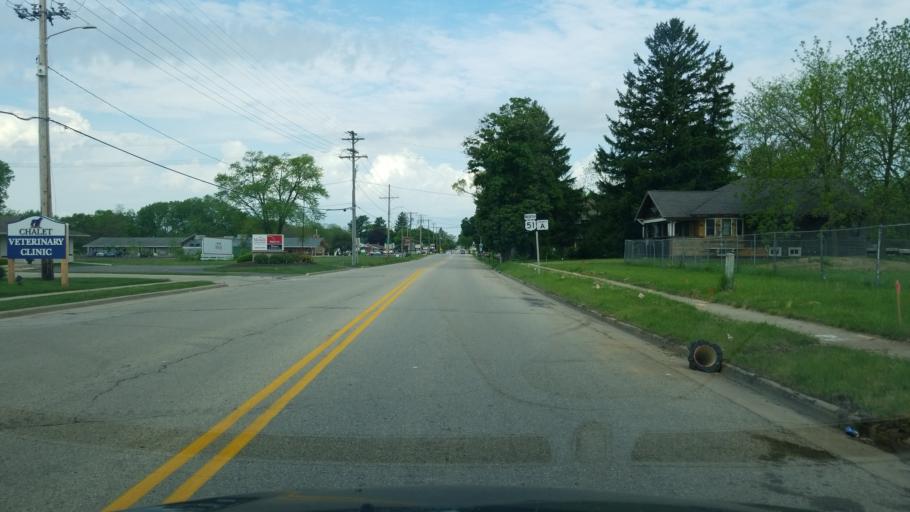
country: US
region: Wisconsin
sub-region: Dane County
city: Stoughton
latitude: 42.9186
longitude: -89.2010
